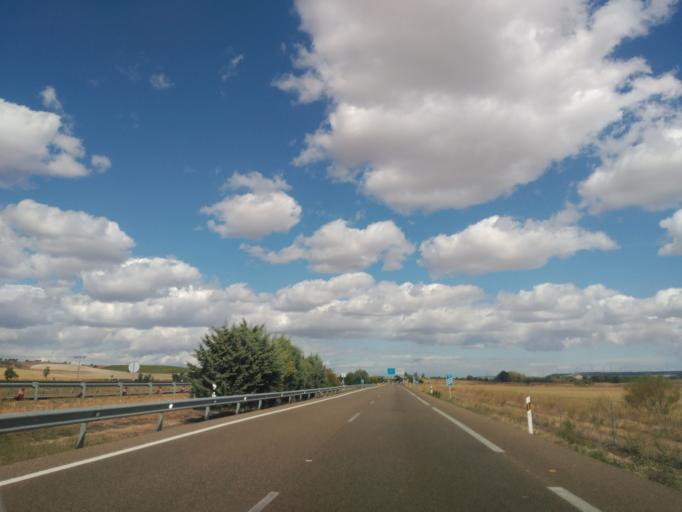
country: ES
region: Castille and Leon
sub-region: Provincia de Palencia
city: Reinoso de Cerrato
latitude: 42.0005
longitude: -4.3782
